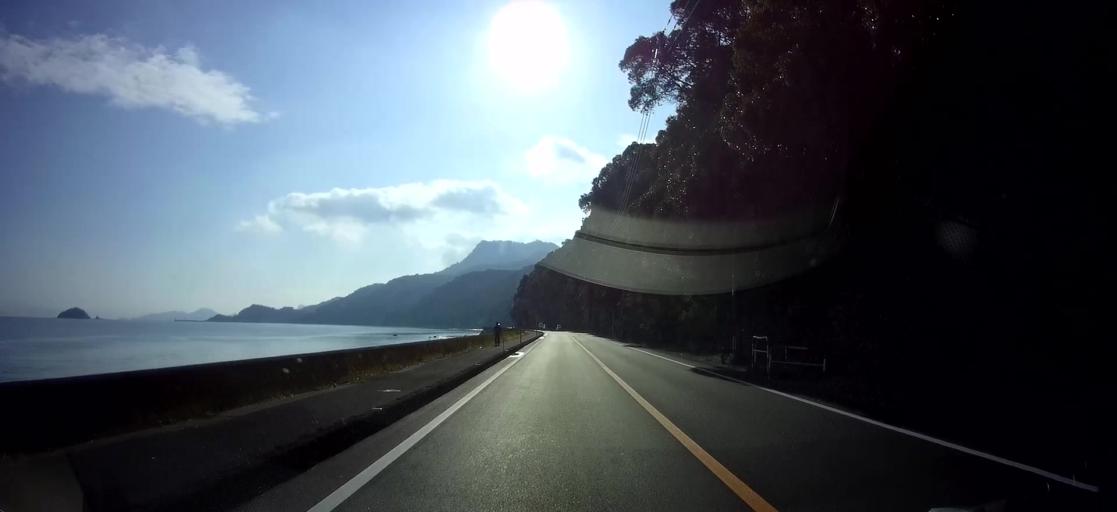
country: JP
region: Kumamoto
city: Yatsushiro
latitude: 32.4924
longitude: 130.4425
